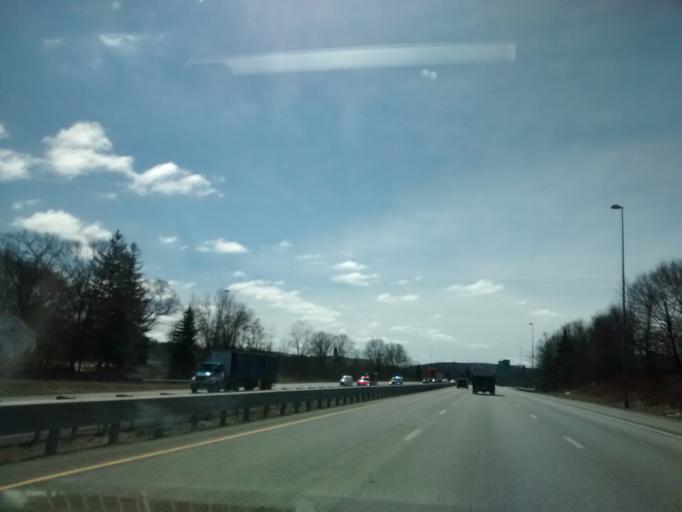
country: US
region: Massachusetts
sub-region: Worcester County
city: Auburn
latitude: 42.2049
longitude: -71.8399
